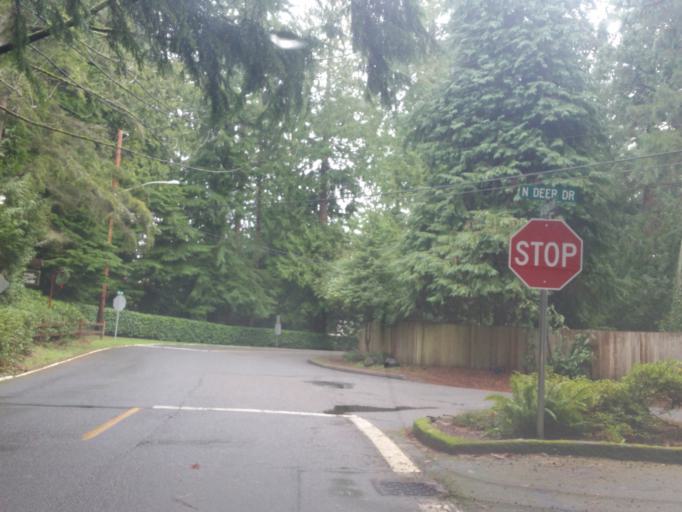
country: US
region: Washington
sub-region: Snohomish County
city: Woodway
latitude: 47.7940
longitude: -122.3774
